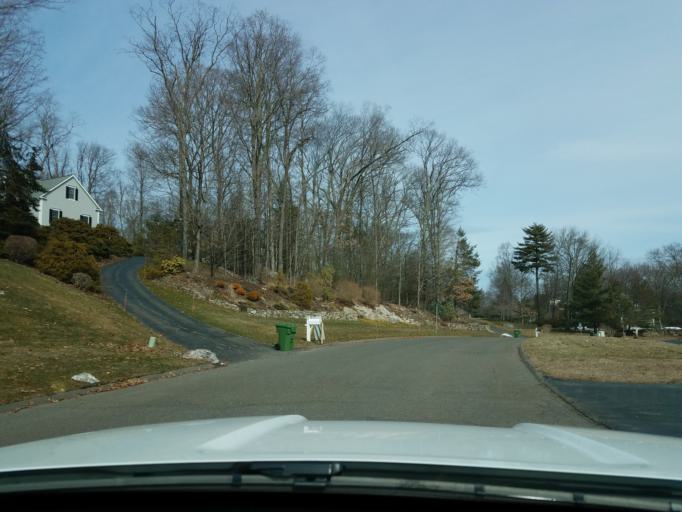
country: US
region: Connecticut
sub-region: Hartford County
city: Collinsville
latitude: 41.8072
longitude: -72.9116
